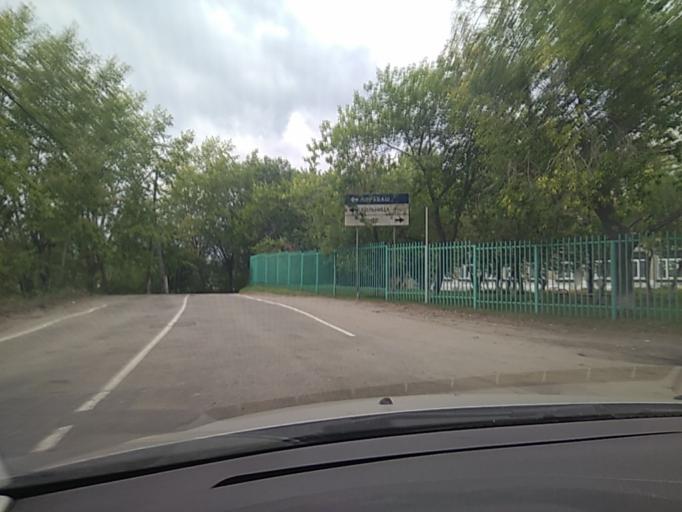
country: RU
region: Chelyabinsk
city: Kyshtym
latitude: 55.7026
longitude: 60.5305
